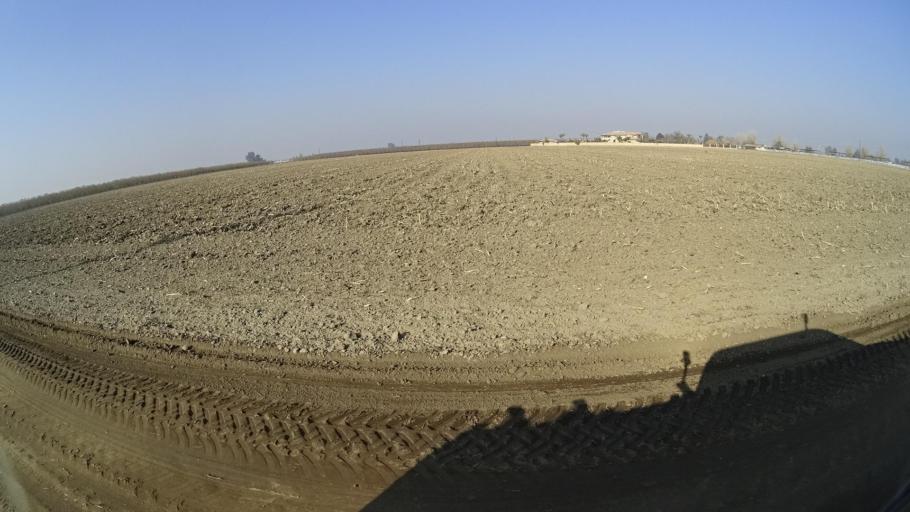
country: US
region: California
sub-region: Kern County
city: Greenfield
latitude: 35.2517
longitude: -119.0415
